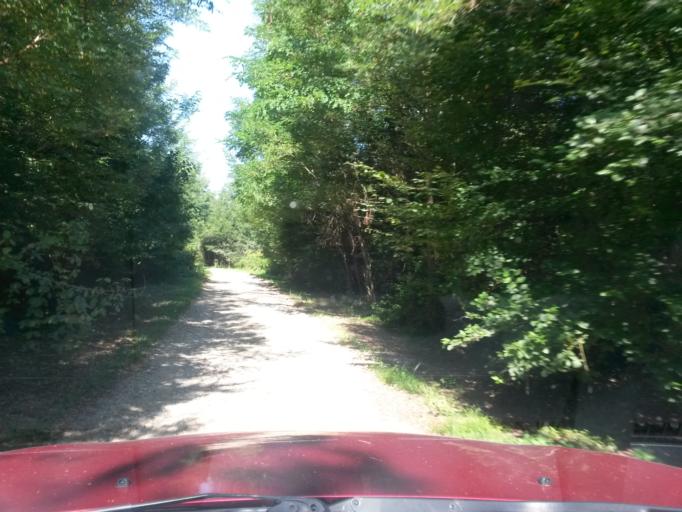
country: HU
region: Borsod-Abauj-Zemplen
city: Gonc
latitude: 48.5230
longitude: 21.2014
